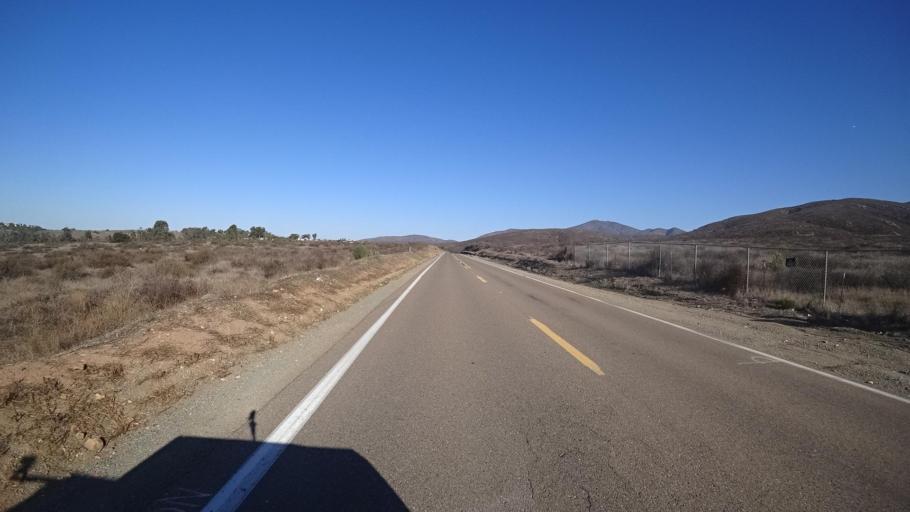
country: US
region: California
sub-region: San Diego County
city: Jamul
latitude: 32.6434
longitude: -116.9256
